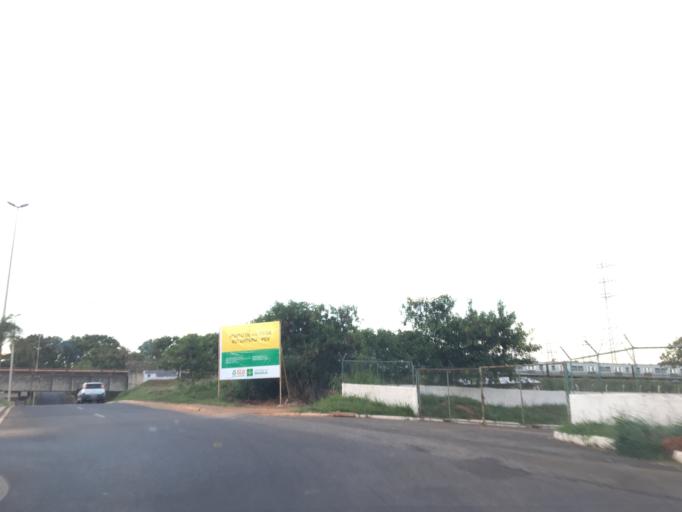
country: BR
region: Federal District
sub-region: Brasilia
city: Brasilia
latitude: -15.8234
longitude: -47.9734
